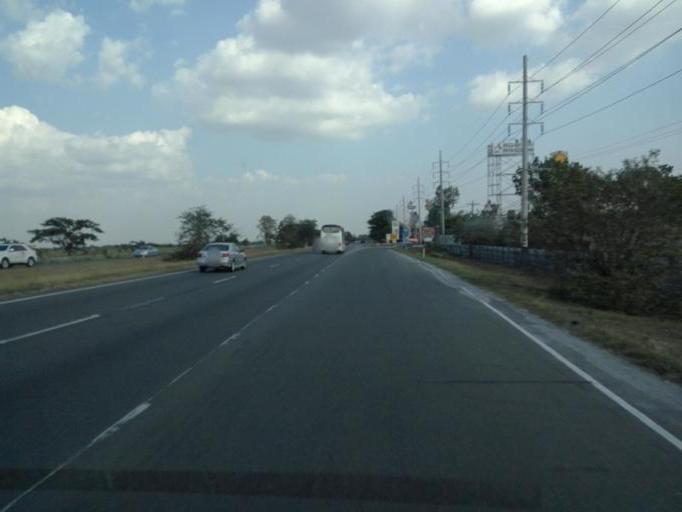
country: PH
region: Central Luzon
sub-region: Province of Pampanga
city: Acli
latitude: 15.1309
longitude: 120.6427
